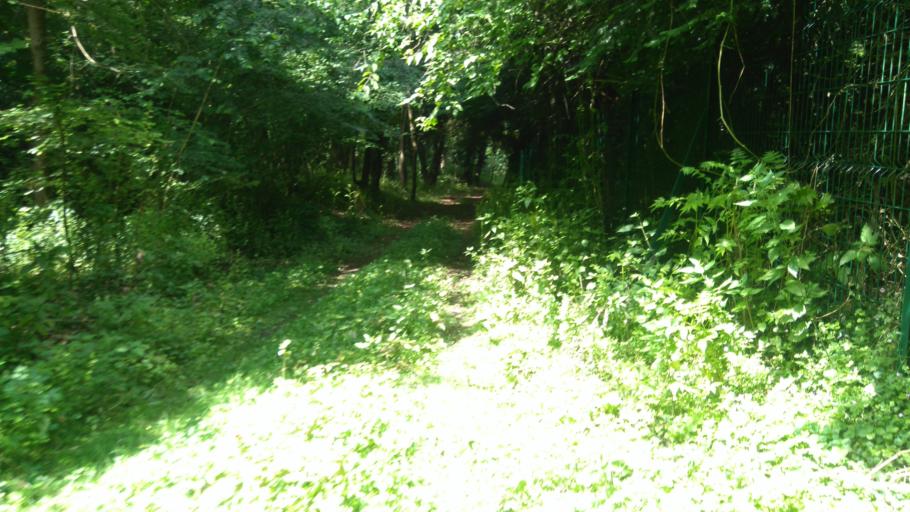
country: FR
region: Picardie
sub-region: Departement de l'Oise
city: Saint-Maximin
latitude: 49.2374
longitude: 2.4516
